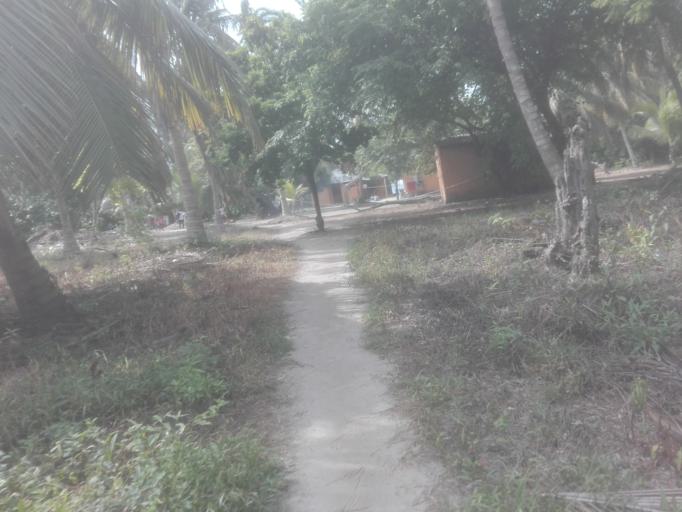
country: CO
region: Bolivar
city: Turbana
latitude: 10.1803
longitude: -75.7314
